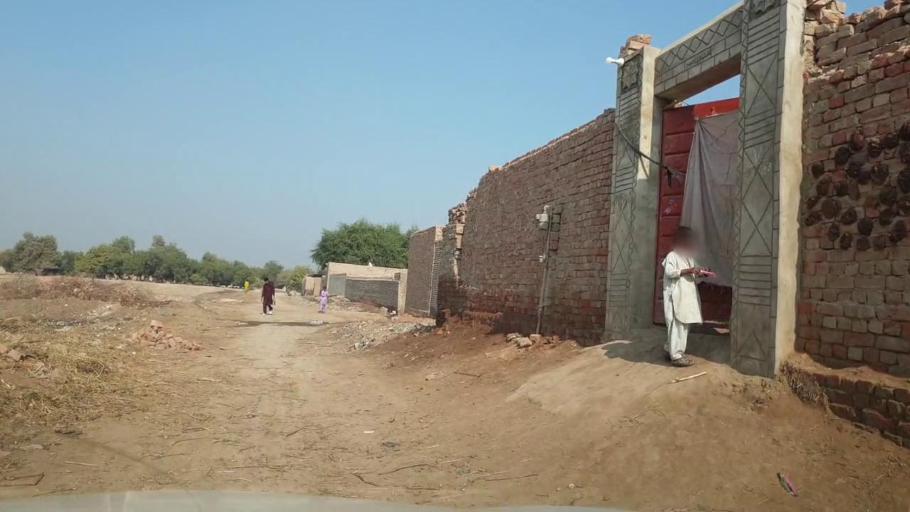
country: PK
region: Sindh
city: Bhan
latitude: 26.5455
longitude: 67.7511
